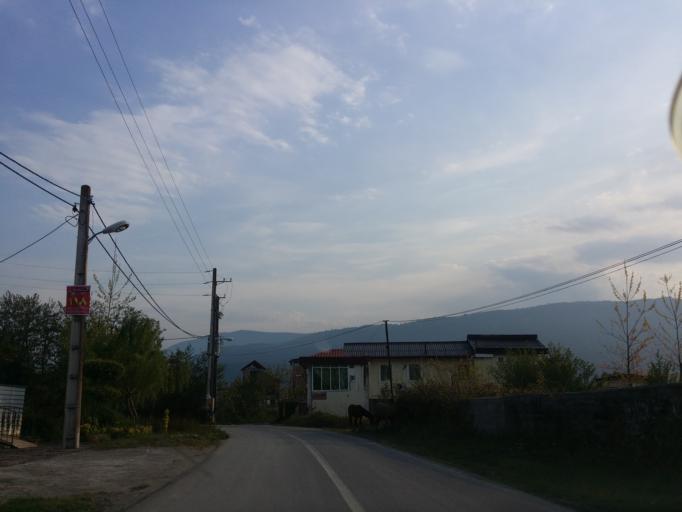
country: IR
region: Mazandaran
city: Chalus
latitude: 36.6825
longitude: 51.3718
